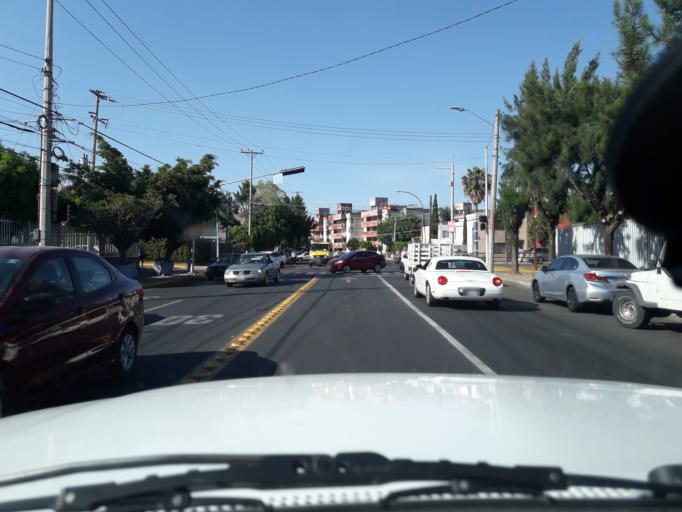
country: MX
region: Jalisco
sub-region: Zapopan
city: Zapopan
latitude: 20.6938
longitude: -103.3517
